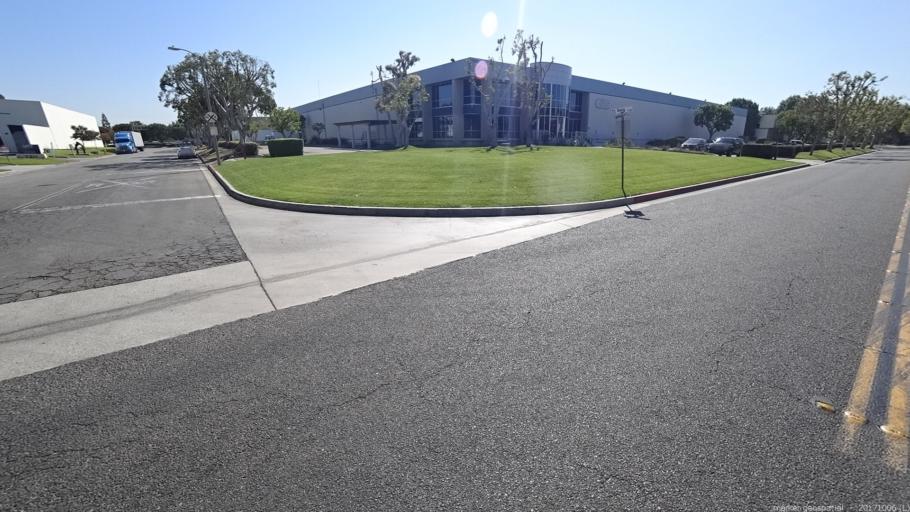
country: US
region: California
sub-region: Orange County
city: Stanton
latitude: 33.7932
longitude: -118.0068
